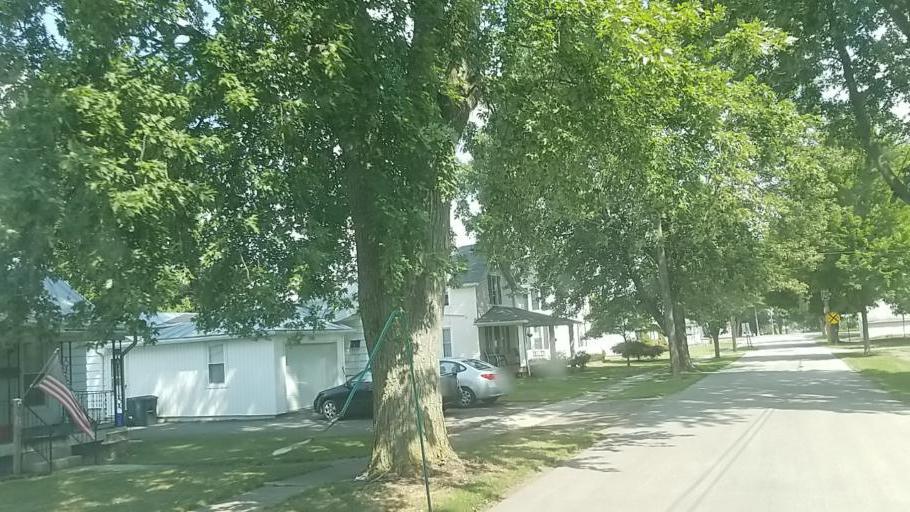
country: US
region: Ohio
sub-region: Wyandot County
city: Upper Sandusky
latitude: 40.8237
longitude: -83.2882
